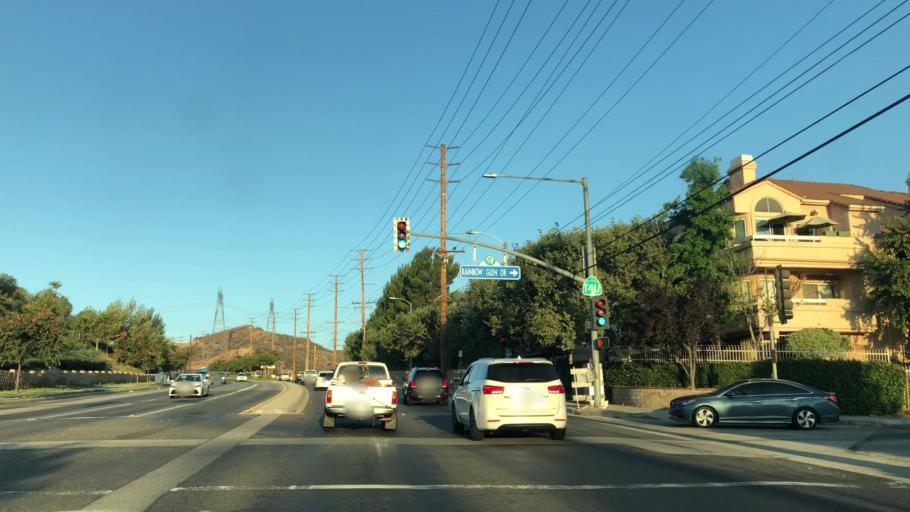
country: US
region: California
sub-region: Los Angeles County
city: Santa Clarita
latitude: 34.3978
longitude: -118.4804
